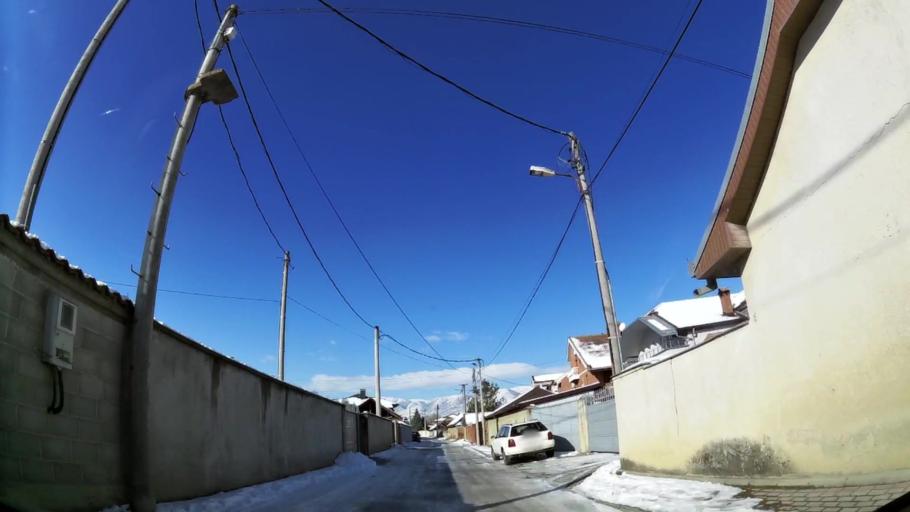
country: MK
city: Ljubin
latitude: 42.0020
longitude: 21.3143
